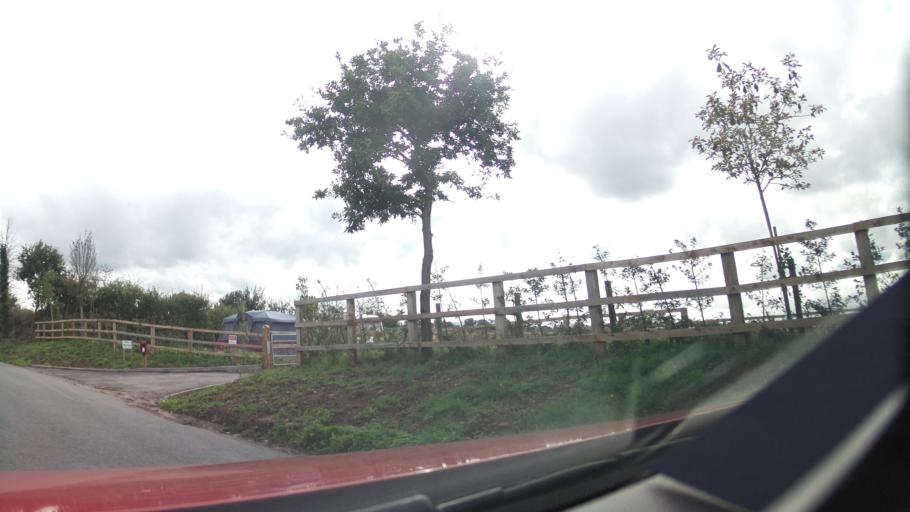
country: GB
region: England
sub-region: Worcestershire
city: Kidderminster
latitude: 52.3548
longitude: -2.1914
